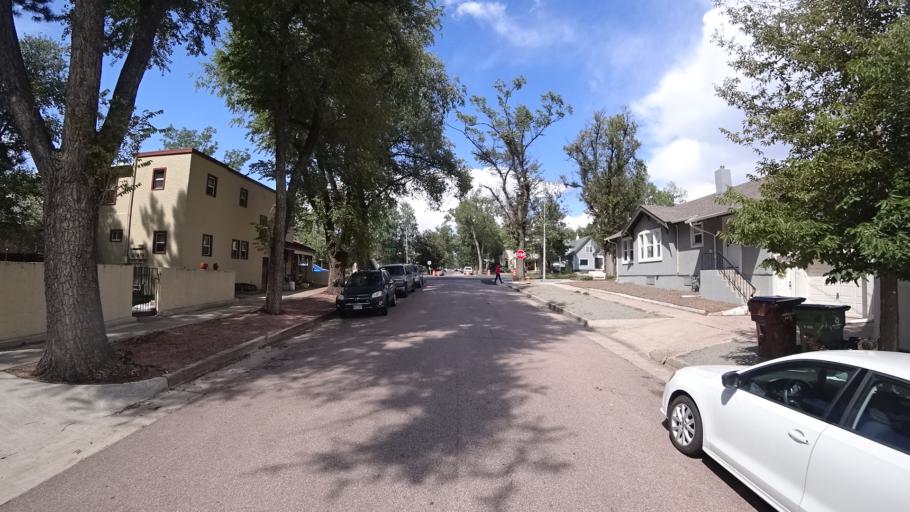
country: US
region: Colorado
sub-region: El Paso County
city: Colorado Springs
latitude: 38.8372
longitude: -104.8104
